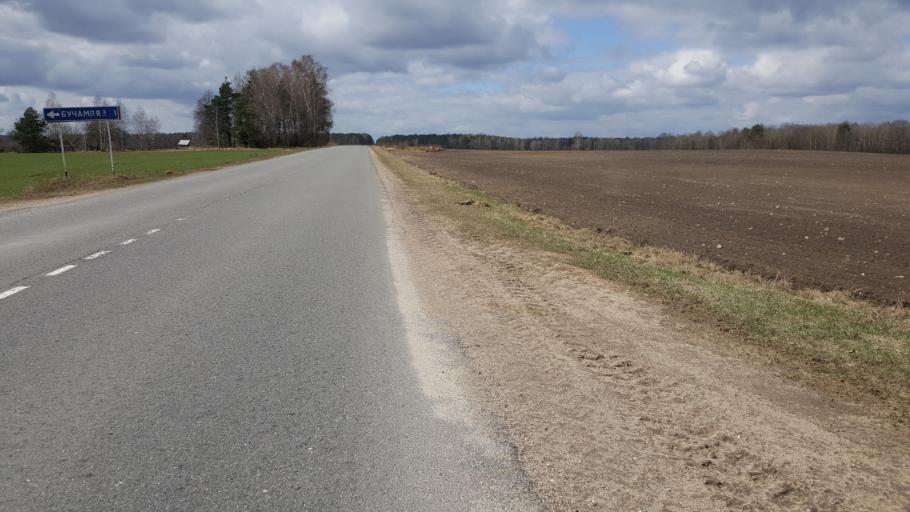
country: BY
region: Brest
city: Kamyanyets
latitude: 52.3791
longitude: 23.6418
